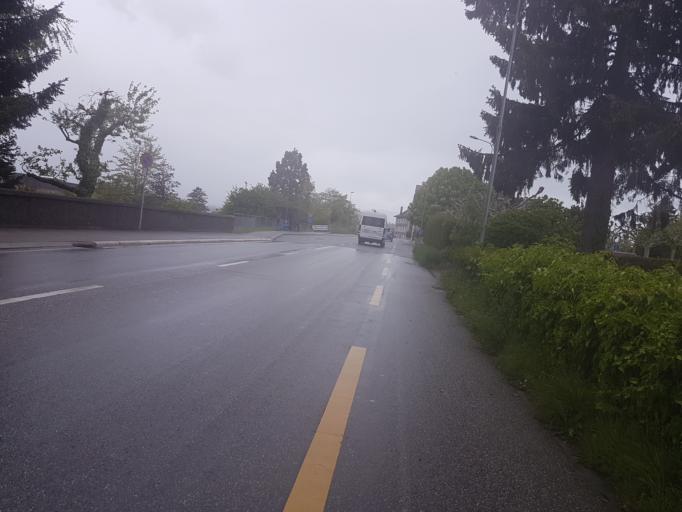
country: CH
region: Vaud
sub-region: Morges District
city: Preverenges
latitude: 46.5172
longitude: 6.5269
